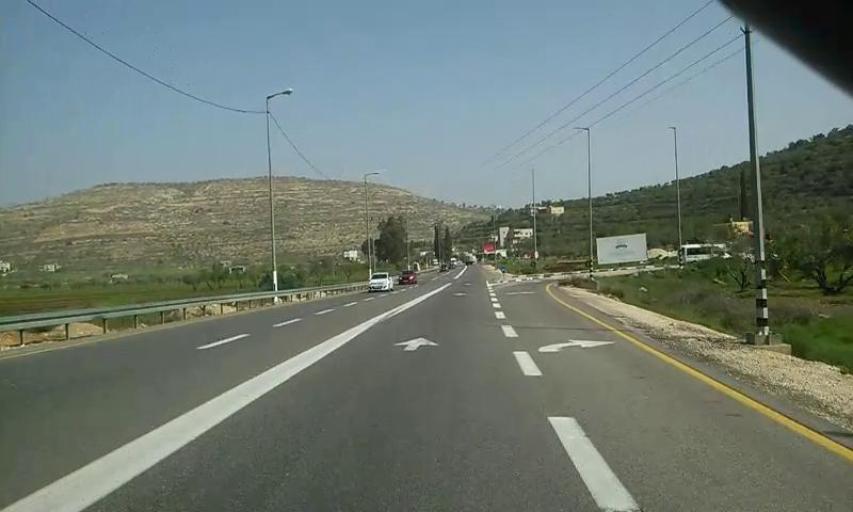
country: PS
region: West Bank
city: Al Lubban ash Sharqiyah
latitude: 32.0723
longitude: 35.2488
